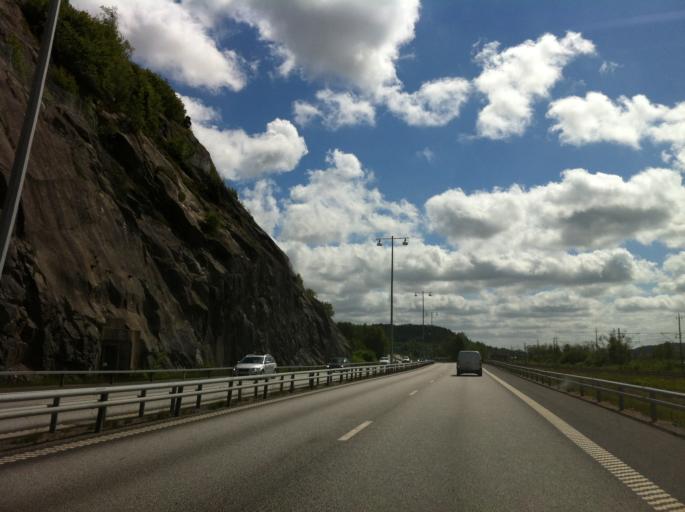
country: SE
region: Vaestra Goetaland
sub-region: Ale Kommun
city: Surte
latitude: 57.8389
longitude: 12.0132
